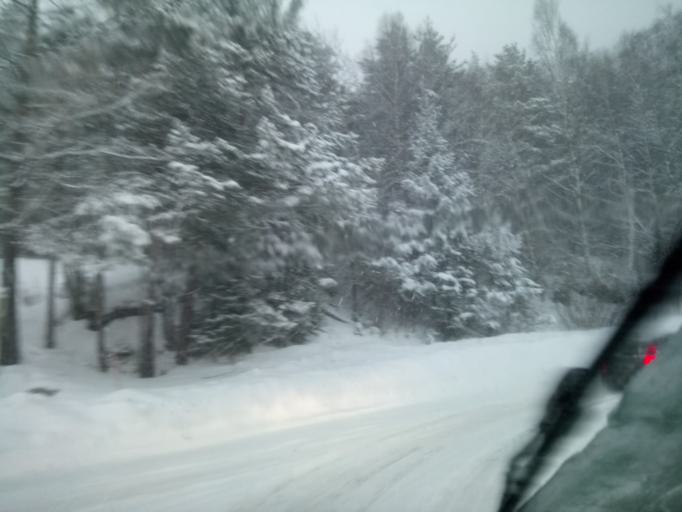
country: FR
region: Rhone-Alpes
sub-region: Departement de la Savoie
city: Modane
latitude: 45.2055
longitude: 6.7053
